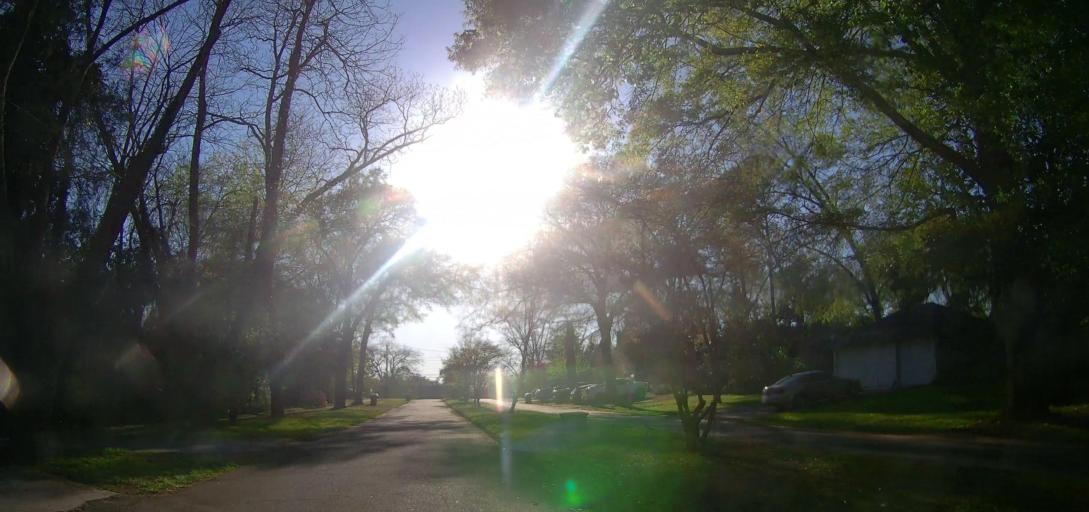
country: US
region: Georgia
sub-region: Baldwin County
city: Milledgeville
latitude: 33.0778
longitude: -83.2302
